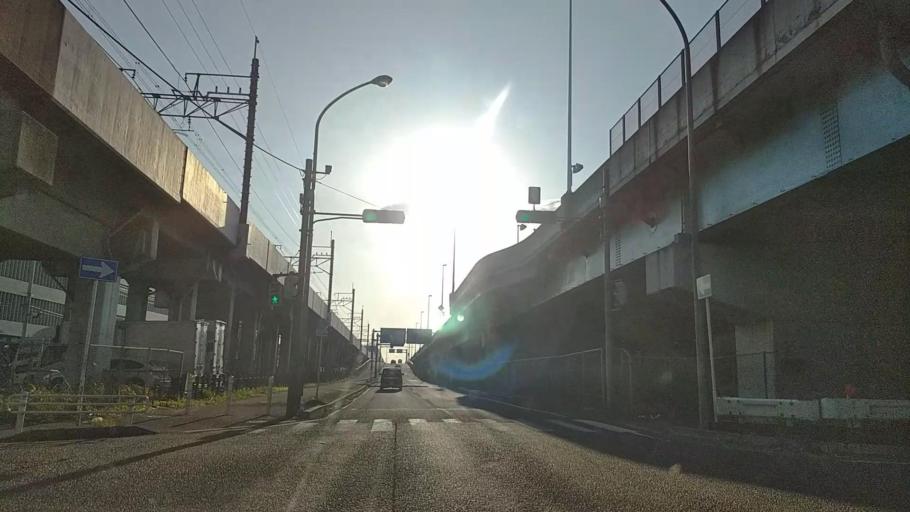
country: JP
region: Tokyo
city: Urayasu
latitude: 35.6781
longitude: 139.9345
